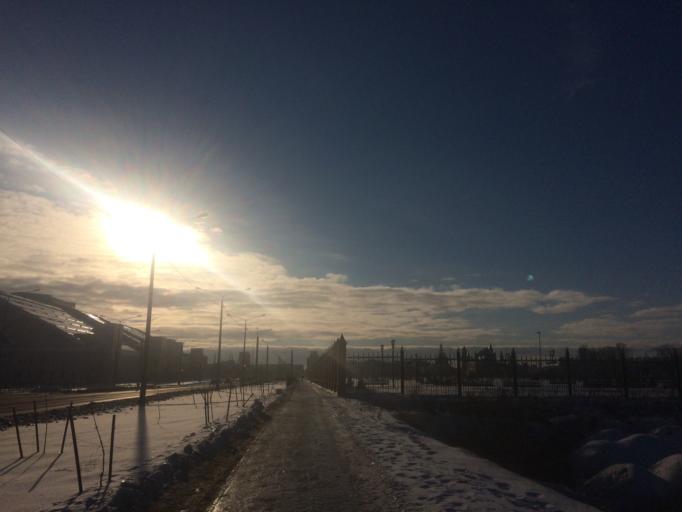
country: RU
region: Mariy-El
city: Yoshkar-Ola
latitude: 56.6423
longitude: 47.9161
